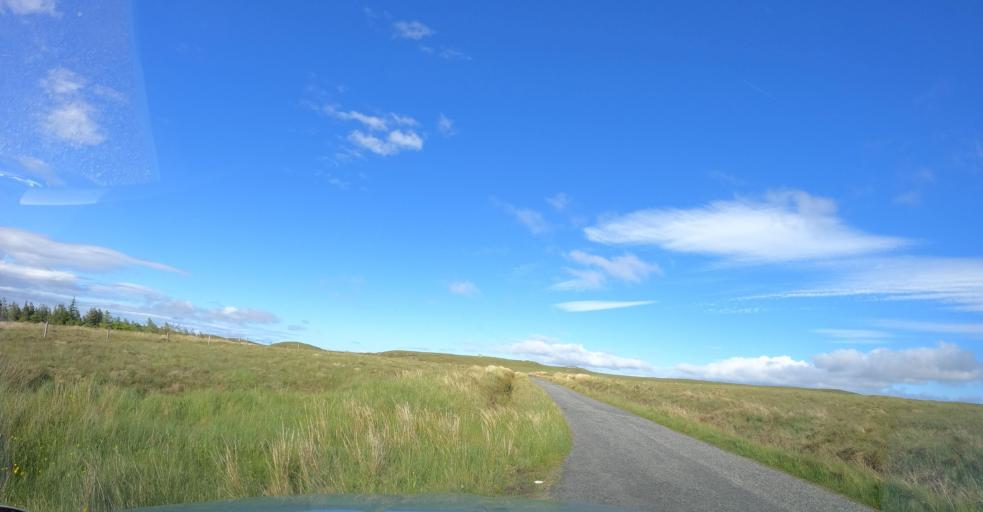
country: GB
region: Scotland
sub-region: Eilean Siar
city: Stornoway
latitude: 58.1803
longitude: -6.5433
